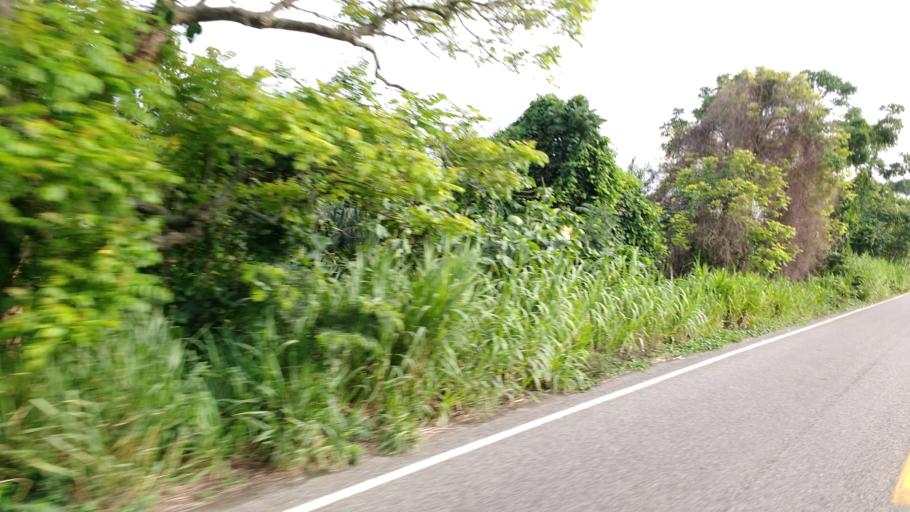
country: MX
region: Tabasco
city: Rio de Teapa
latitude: 17.6883
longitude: -92.9445
